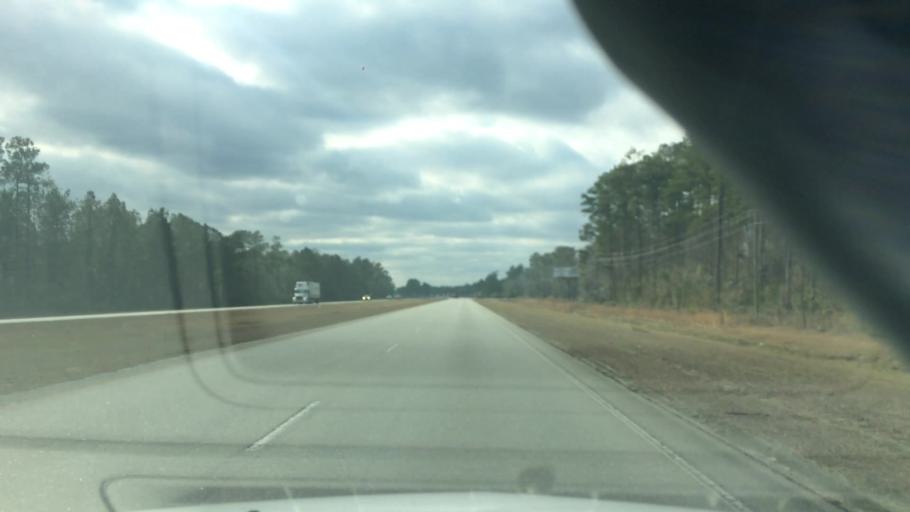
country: US
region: North Carolina
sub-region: Brunswick County
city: Bolivia
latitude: 34.0422
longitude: -78.2399
